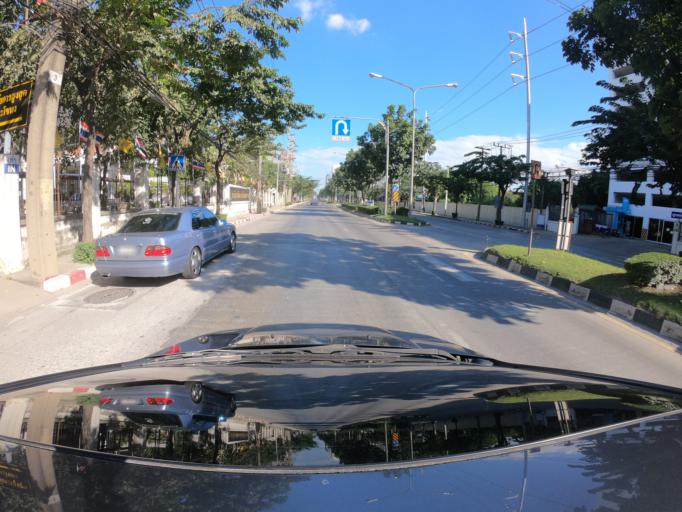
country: TH
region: Bangkok
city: Phra Khanong
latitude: 13.6758
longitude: 100.5931
